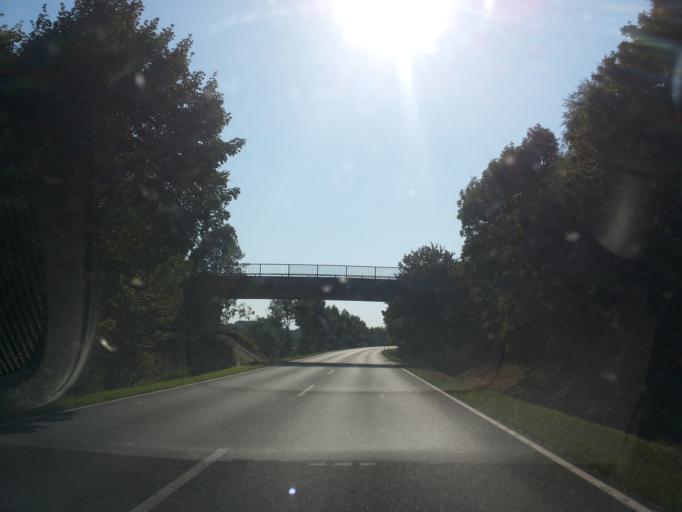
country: DE
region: Bavaria
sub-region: Lower Bavaria
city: Neustadt an der Donau
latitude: 48.8179
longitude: 11.7170
